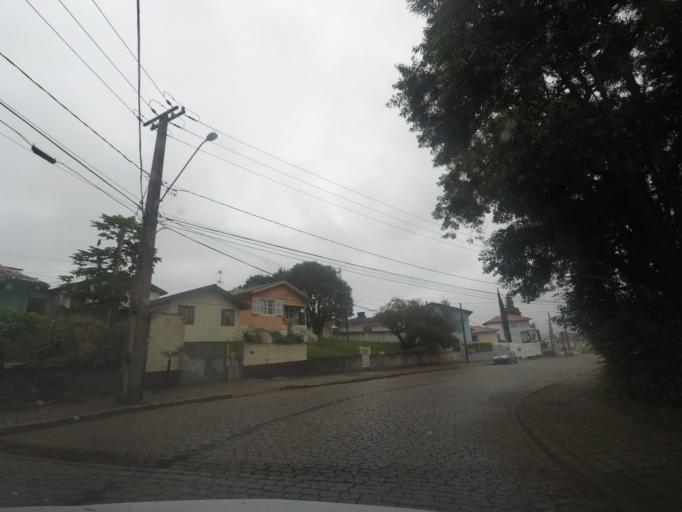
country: BR
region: Parana
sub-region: Quatro Barras
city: Quatro Barras
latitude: -25.3705
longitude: -49.0763
